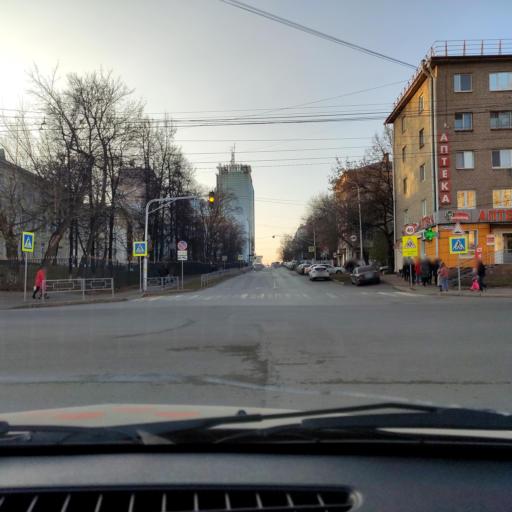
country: RU
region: Bashkortostan
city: Ufa
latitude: 54.7767
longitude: 56.0354
